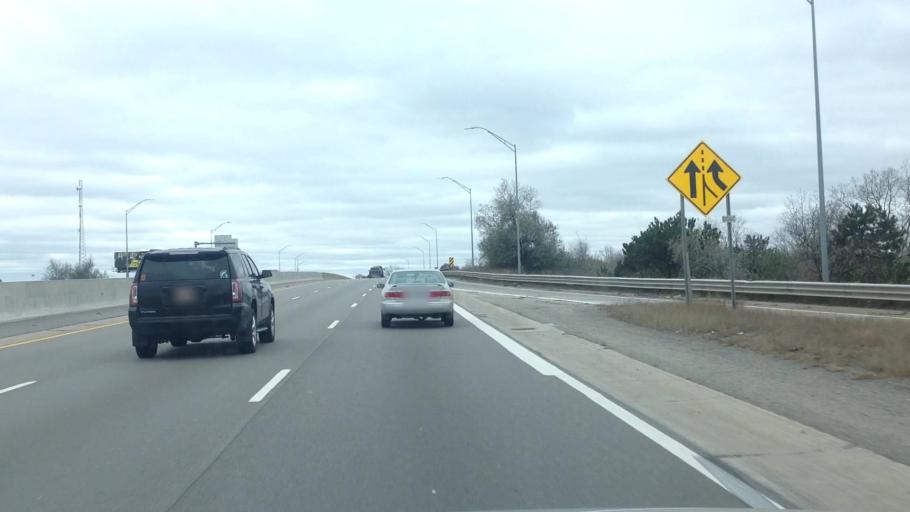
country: US
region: Michigan
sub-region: Genesee County
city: Flint
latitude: 43.0120
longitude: -83.6574
